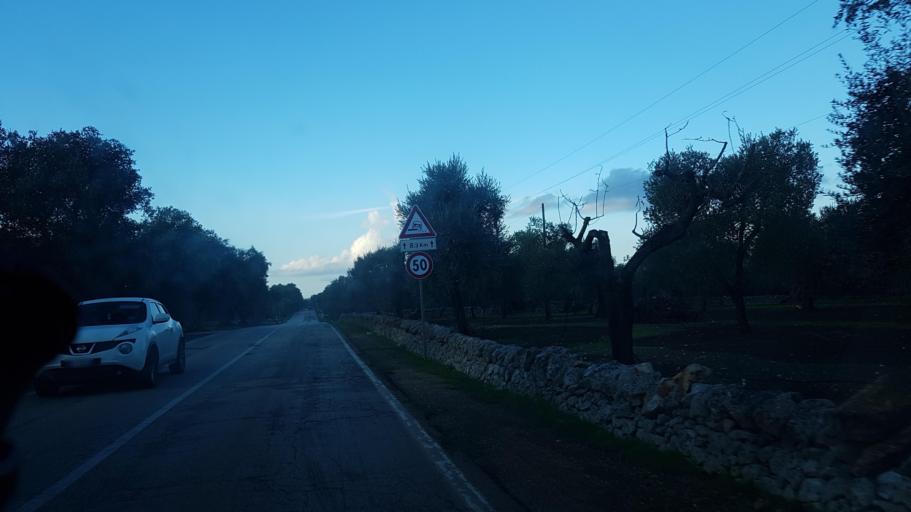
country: IT
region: Apulia
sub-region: Provincia di Brindisi
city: San Michele Salentino
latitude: 40.6500
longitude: 17.6061
